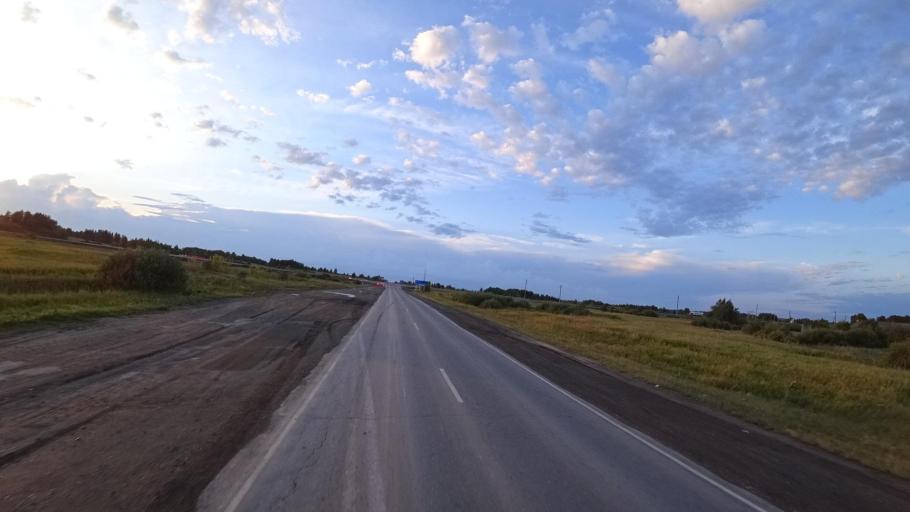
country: RU
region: Sverdlovsk
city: Kamyshlov
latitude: 56.8752
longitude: 62.7119
